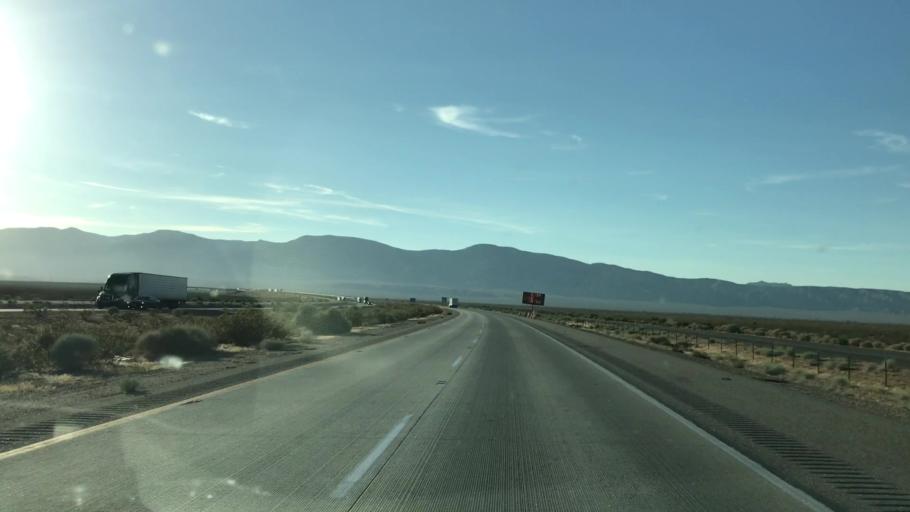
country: US
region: California
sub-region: Kern County
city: Mojave
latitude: 35.0842
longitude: -118.1189
